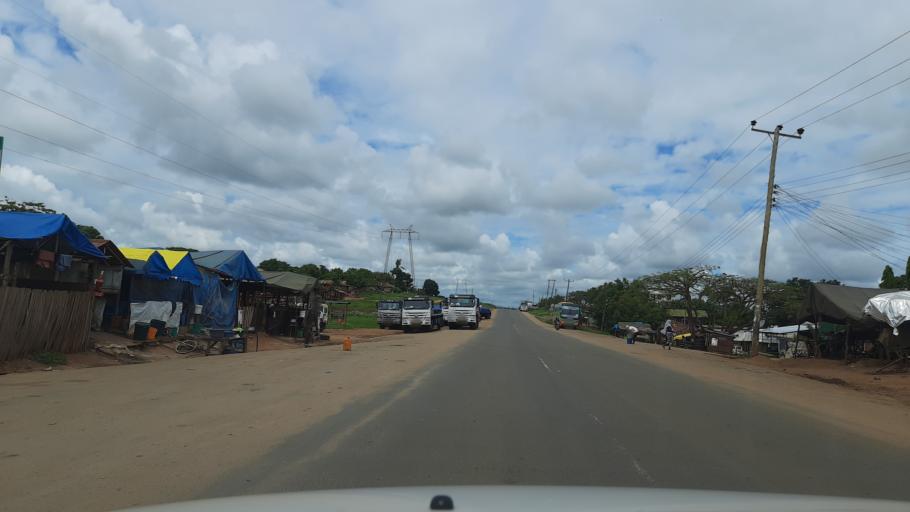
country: TZ
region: Tanga
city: Chanika
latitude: -5.7852
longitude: 38.2918
